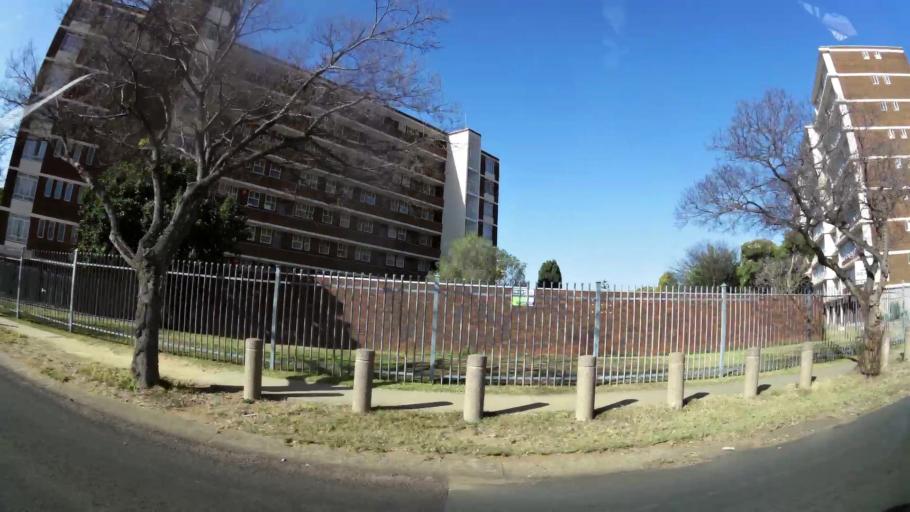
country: ZA
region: Gauteng
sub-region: City of Tshwane Metropolitan Municipality
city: Pretoria
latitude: -25.7292
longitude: 28.2459
